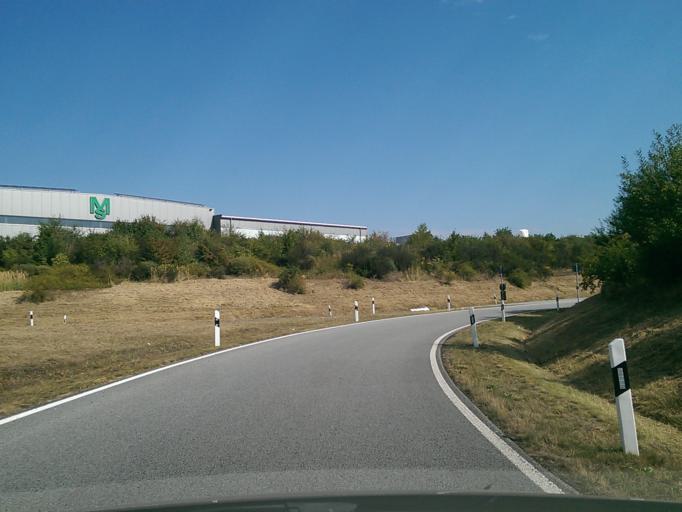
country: DE
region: Saxony
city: Zittau
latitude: 50.9071
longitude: 14.8357
